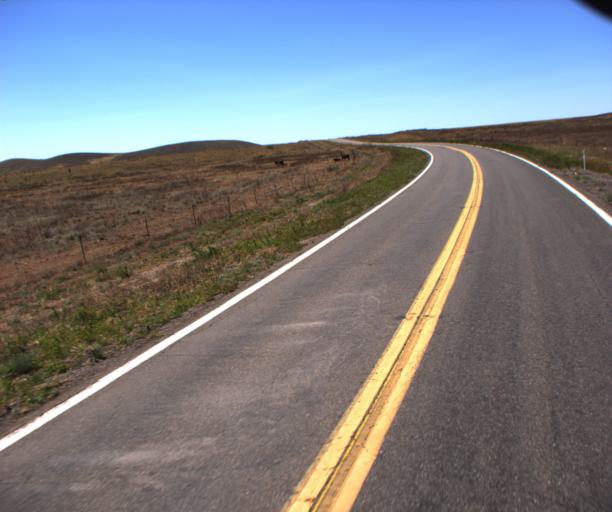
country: US
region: Arizona
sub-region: Cochise County
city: Douglas
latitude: 31.6202
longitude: -109.2136
